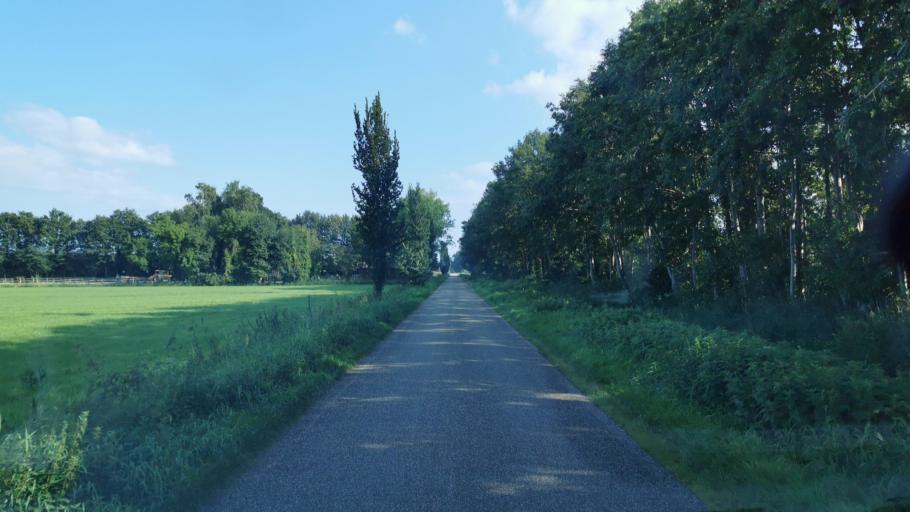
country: NL
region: Overijssel
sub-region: Gemeente Borne
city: Borne
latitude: 52.3311
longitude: 6.7694
